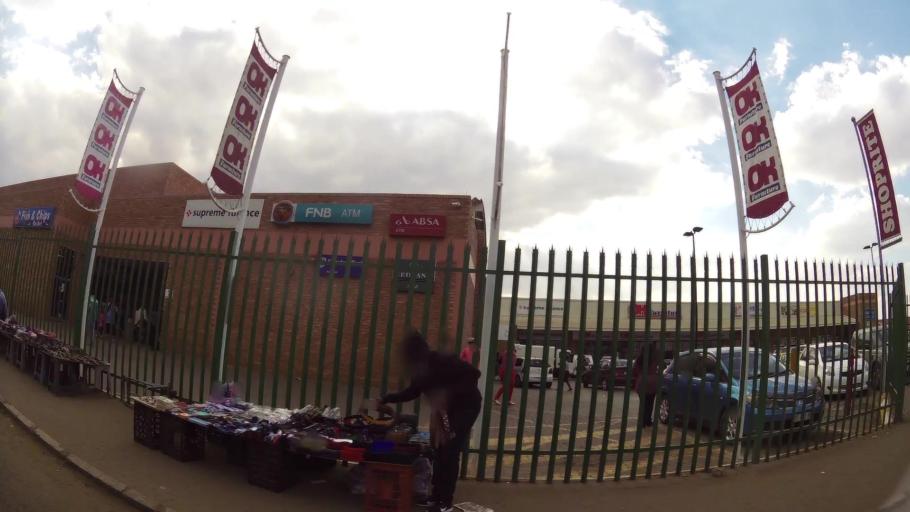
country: ZA
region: Mpumalanga
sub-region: Nkangala District Municipality
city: Delmas
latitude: -26.1511
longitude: 28.6825
